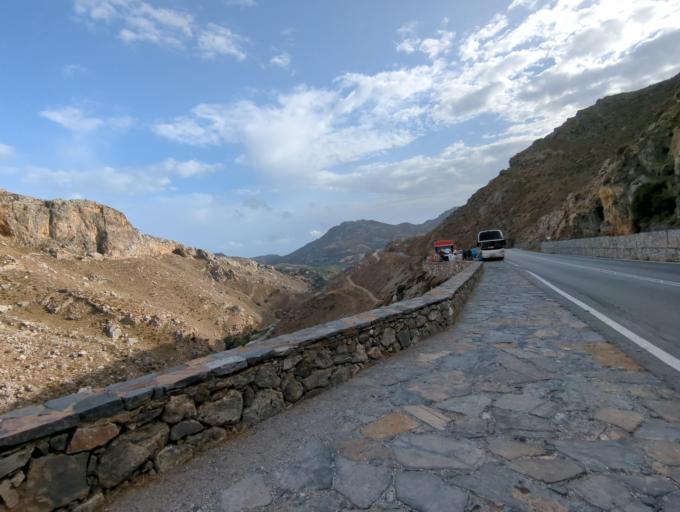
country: GR
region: Crete
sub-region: Nomos Rethymnis
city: Atsipopoulon
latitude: 35.1947
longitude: 24.4640
